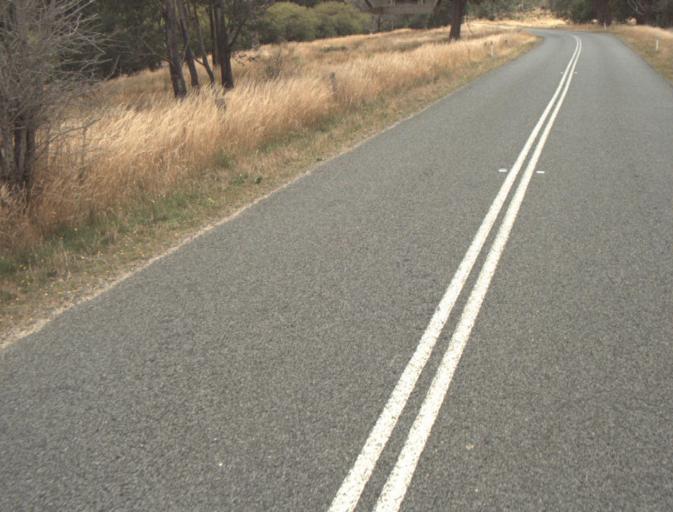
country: AU
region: Tasmania
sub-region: Northern Midlands
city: Evandale
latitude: -41.4980
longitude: 147.4170
